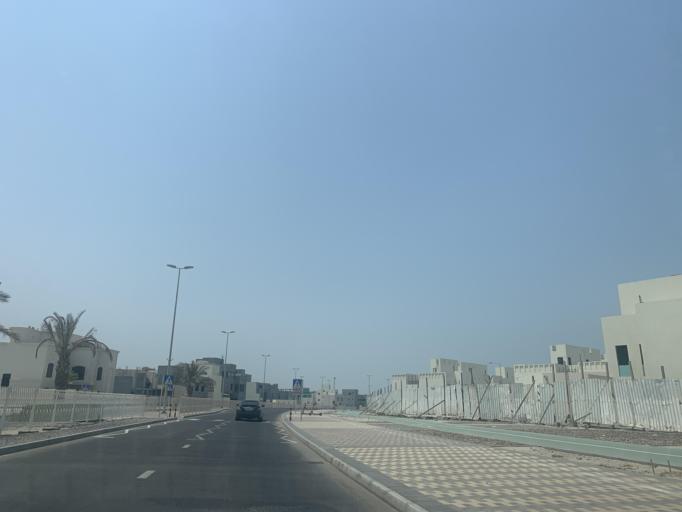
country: BH
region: Muharraq
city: Al Hadd
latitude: 26.2373
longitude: 50.6642
